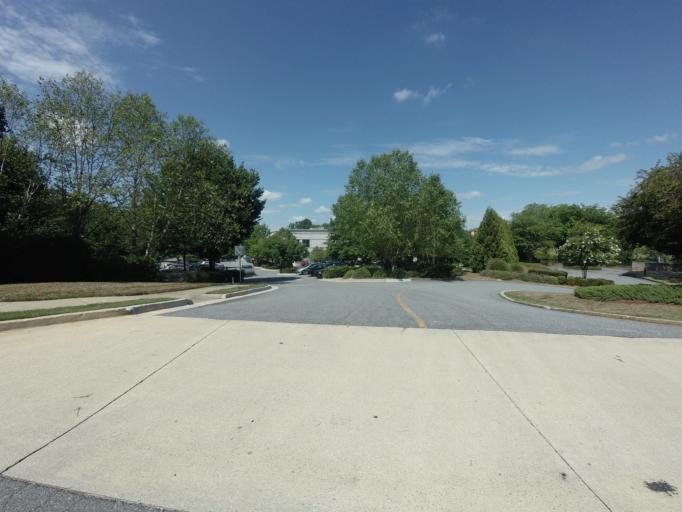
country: US
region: Georgia
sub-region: Fulton County
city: Johns Creek
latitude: 34.0562
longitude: -84.1718
